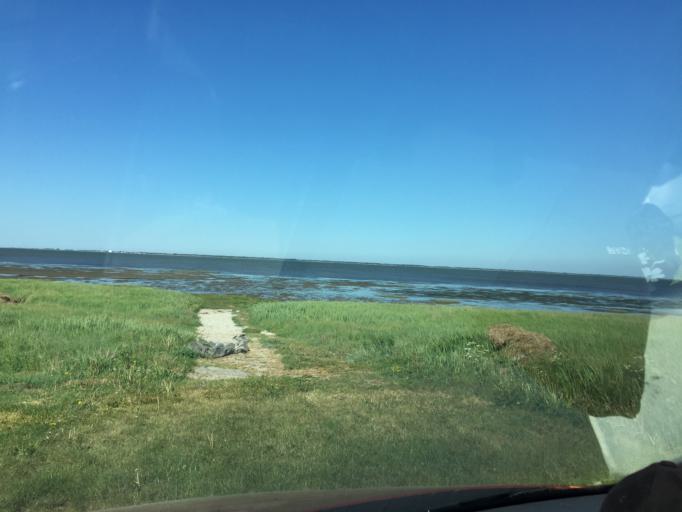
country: DK
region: South Denmark
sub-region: Tonder Kommune
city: Sherrebek
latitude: 55.0909
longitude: 8.6517
